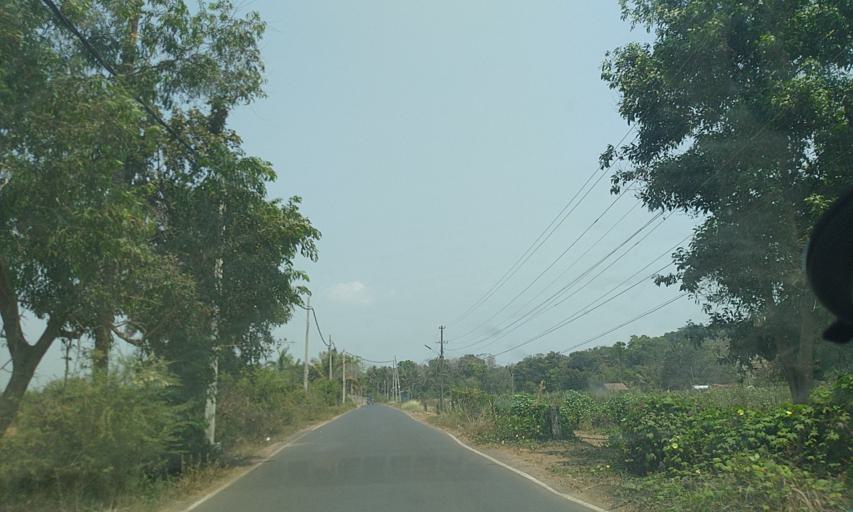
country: IN
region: Goa
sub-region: North Goa
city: Saligao
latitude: 15.5530
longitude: 73.8094
